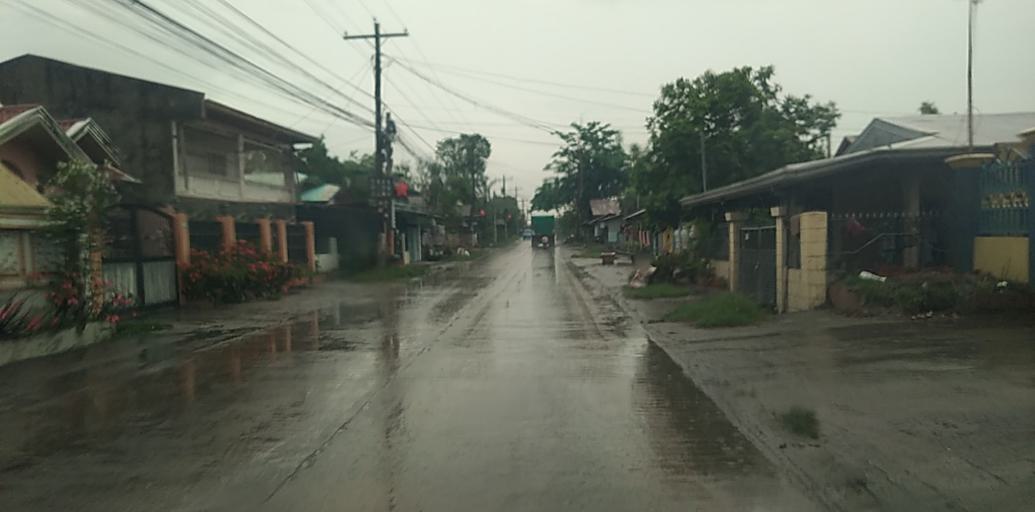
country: PH
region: Central Luzon
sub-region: Province of Pampanga
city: San Antonio
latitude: 15.1555
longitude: 120.6874
